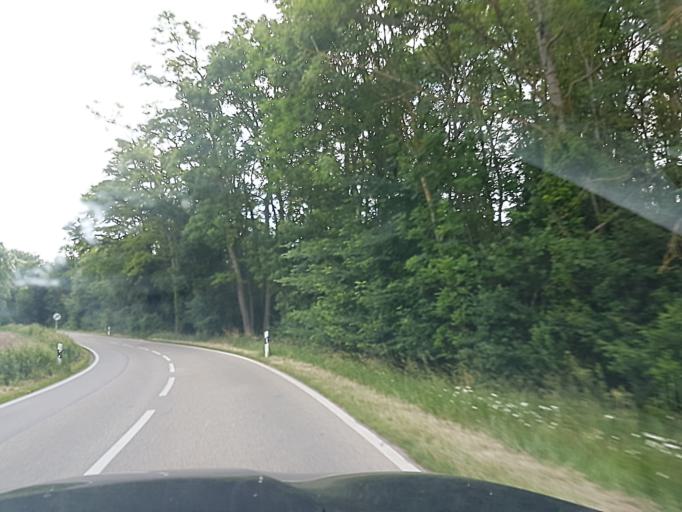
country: DE
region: Baden-Wuerttemberg
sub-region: Freiburg Region
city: Merdingen
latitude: 48.0118
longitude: 7.6684
